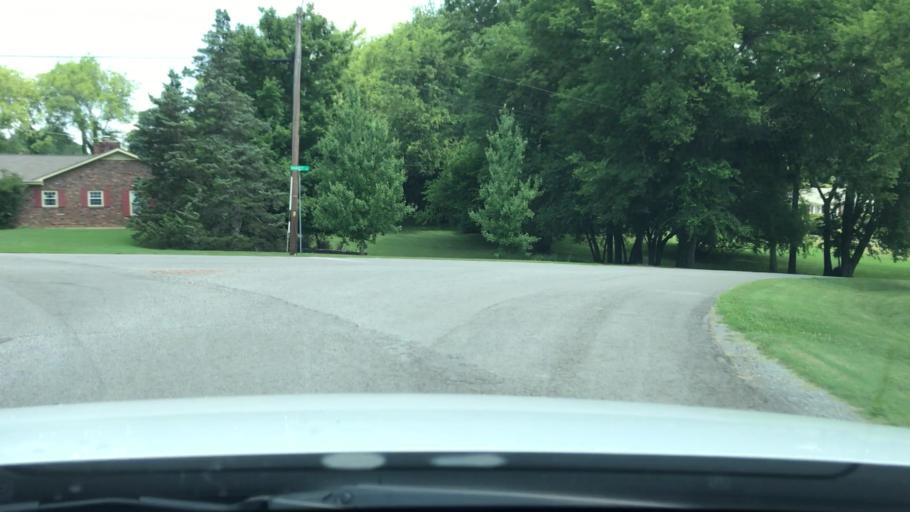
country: US
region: Tennessee
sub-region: Sumner County
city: Gallatin
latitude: 36.3699
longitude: -86.4707
